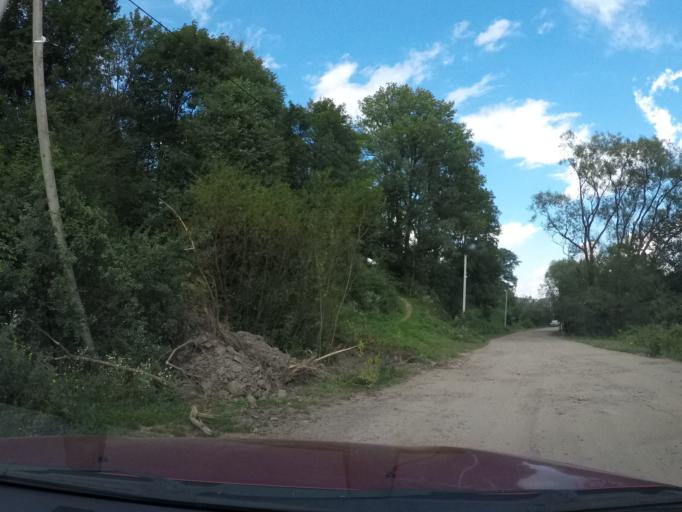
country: UA
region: Zakarpattia
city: Velykyi Bereznyi
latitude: 49.0293
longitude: 22.5890
